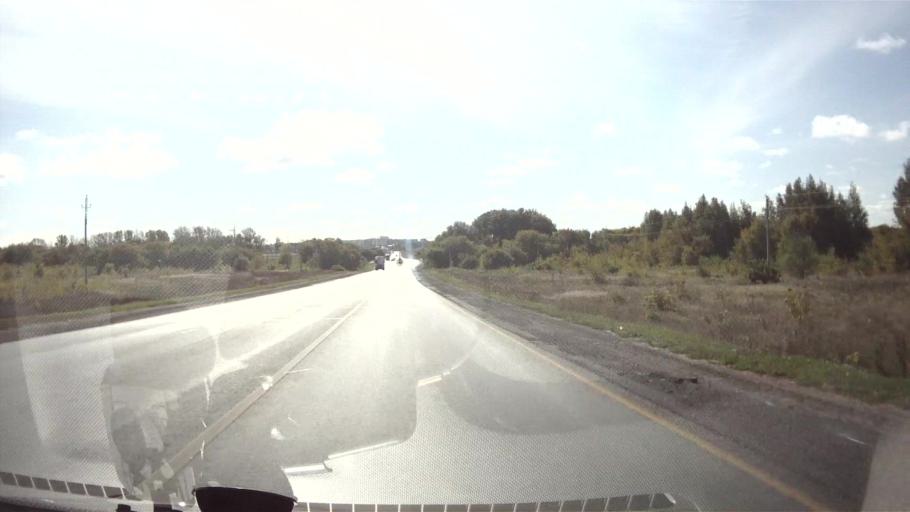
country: RU
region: Ulyanovsk
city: Isheyevka
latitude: 54.3071
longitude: 48.2394
